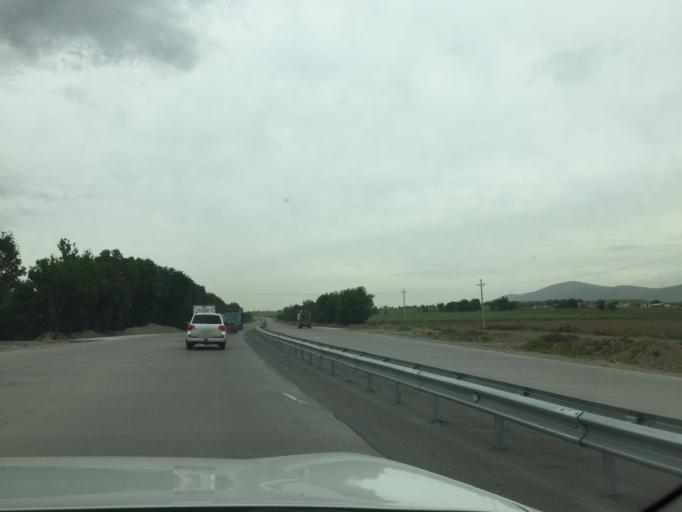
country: KZ
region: Ongtustik Qazaqstan
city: Sastobe
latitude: 42.5029
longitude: 69.9624
